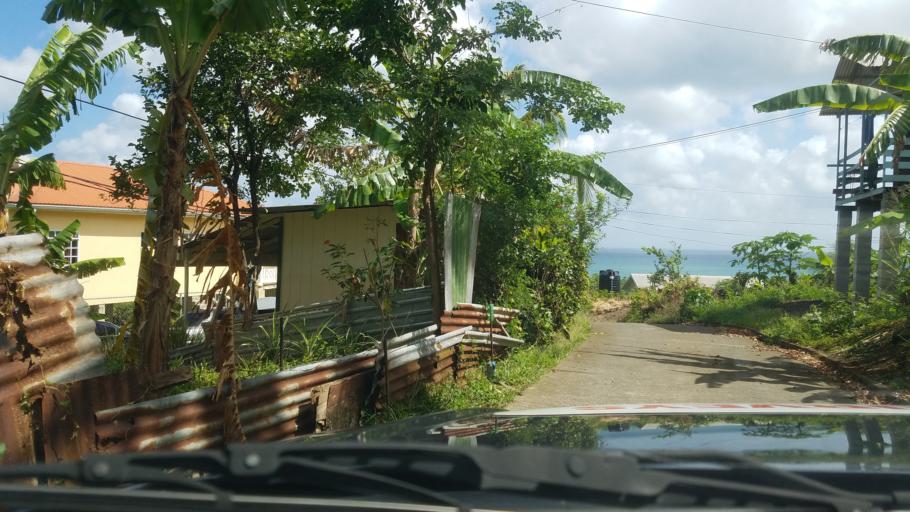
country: LC
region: Castries Quarter
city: Bisee
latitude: 14.0165
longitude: -60.9842
